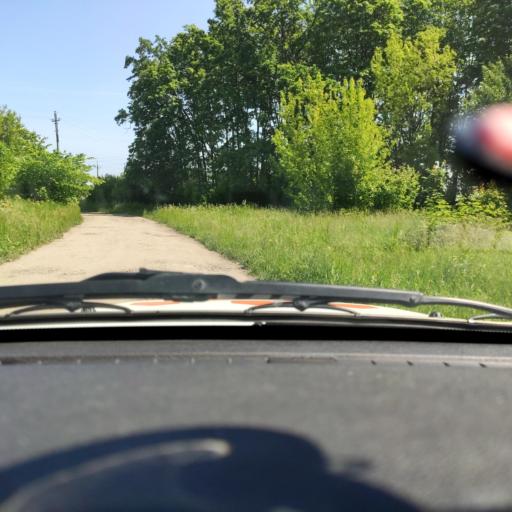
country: RU
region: Voronezj
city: Devitsa
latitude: 51.5928
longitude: 38.9802
